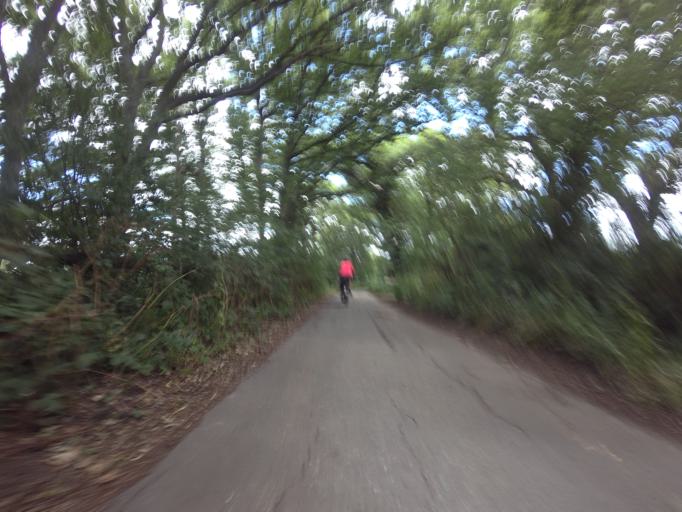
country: GB
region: England
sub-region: East Sussex
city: Hailsham
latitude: 50.8371
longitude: 0.2157
